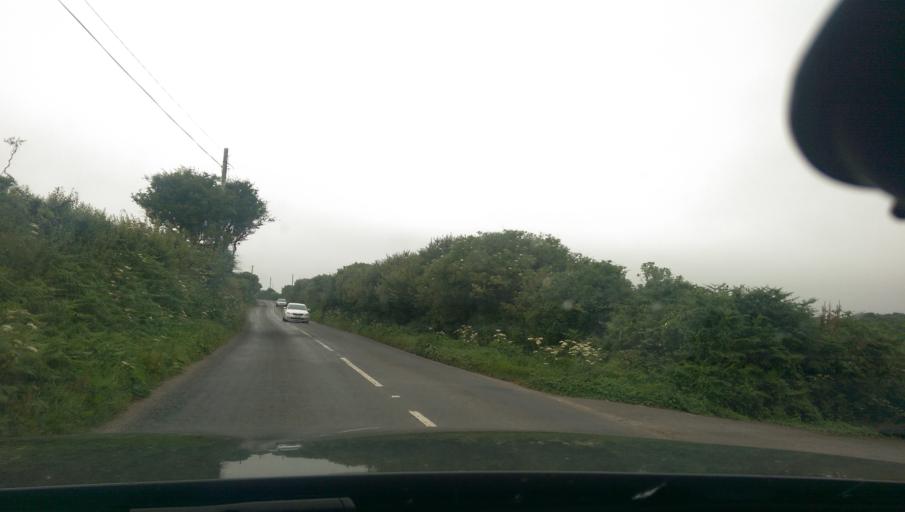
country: GB
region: England
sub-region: Cornwall
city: St. Buryan
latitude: 50.0911
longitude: -5.6279
